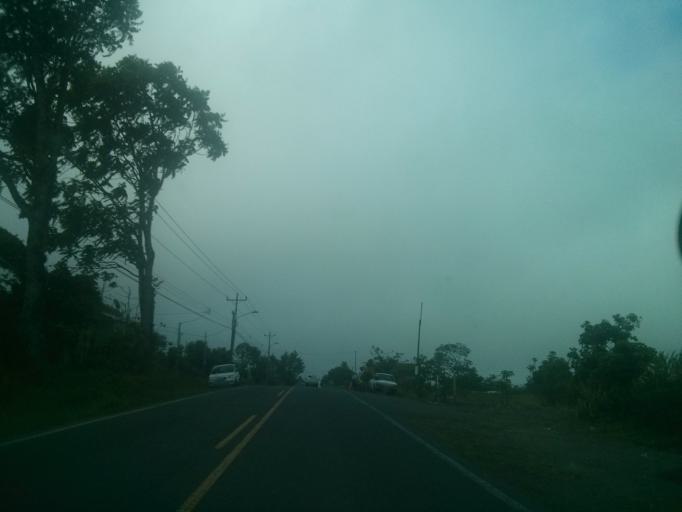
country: CR
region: Cartago
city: Cot
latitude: 9.8779
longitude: -83.8219
